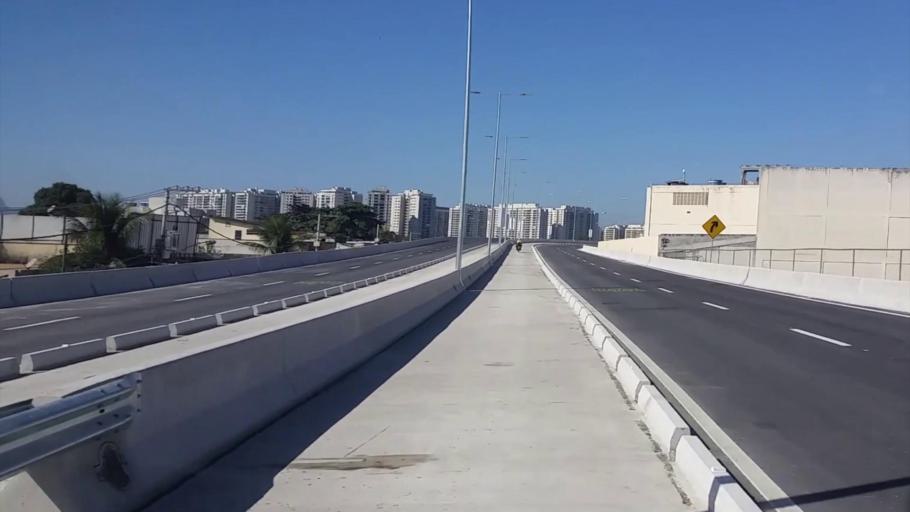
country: BR
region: Rio de Janeiro
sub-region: Nilopolis
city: Nilopolis
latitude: -22.9501
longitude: -43.3901
